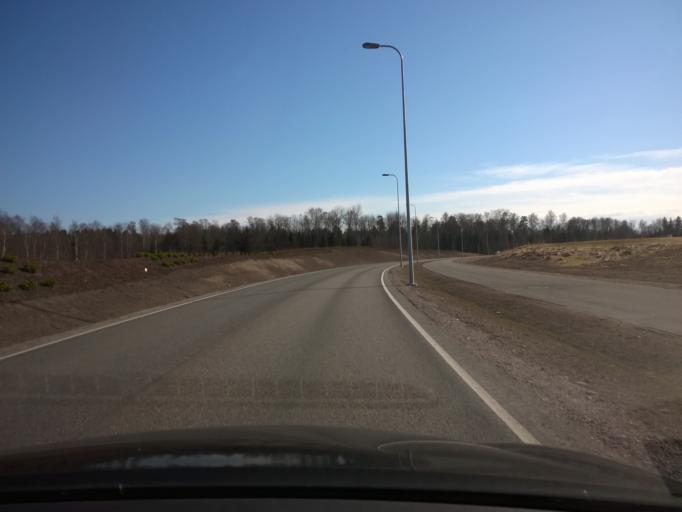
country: FI
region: Uusimaa
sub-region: Helsinki
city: Kilo
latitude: 60.1942
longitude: 24.7893
